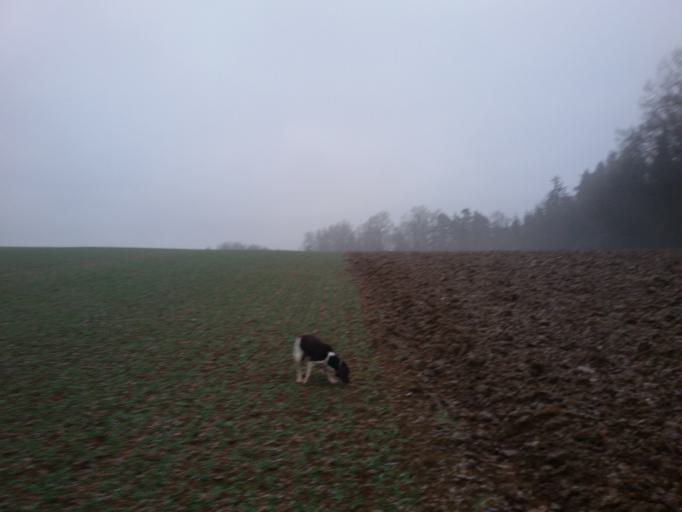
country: DE
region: Bavaria
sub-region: Upper Palatinate
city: Gebenbach
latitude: 49.5163
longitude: 11.8616
